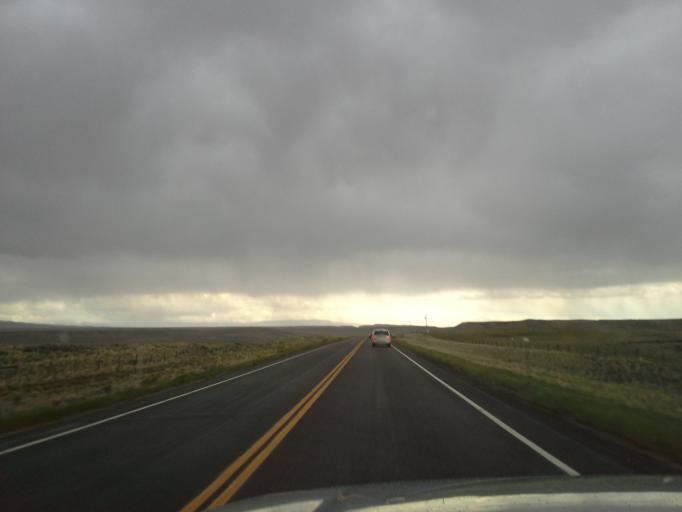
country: US
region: Wyoming
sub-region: Park County
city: Powell
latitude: 45.0712
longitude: -108.6833
